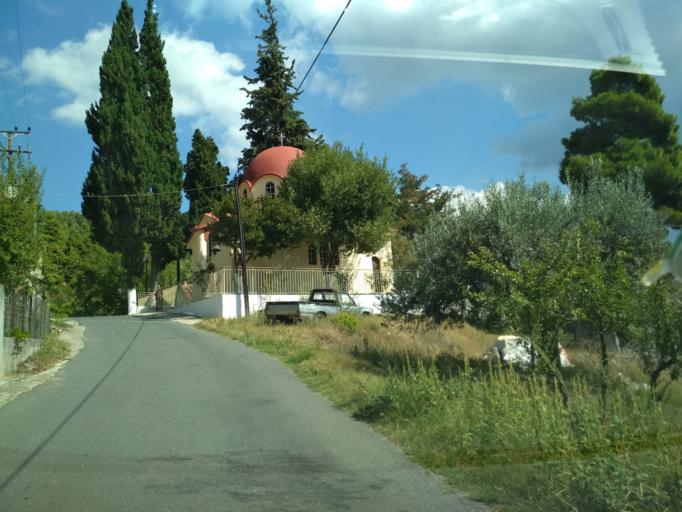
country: GR
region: Central Greece
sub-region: Nomos Evvoias
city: Roviai
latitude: 38.8275
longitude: 23.2807
